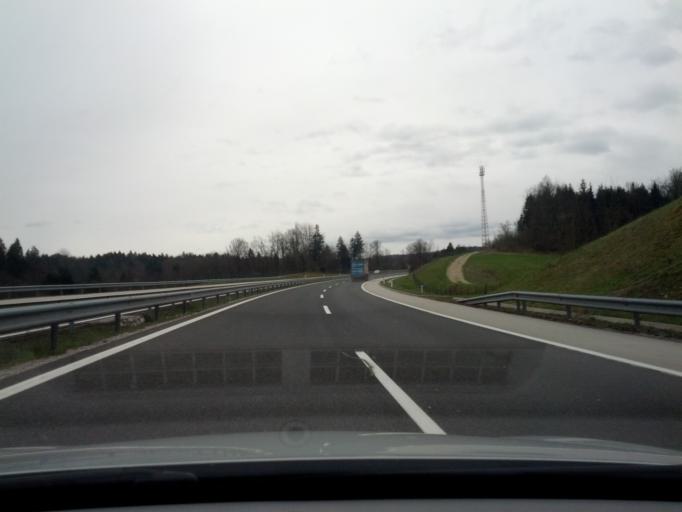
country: SI
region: Trebnje
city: Trebnje
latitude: 45.9193
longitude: 14.9517
